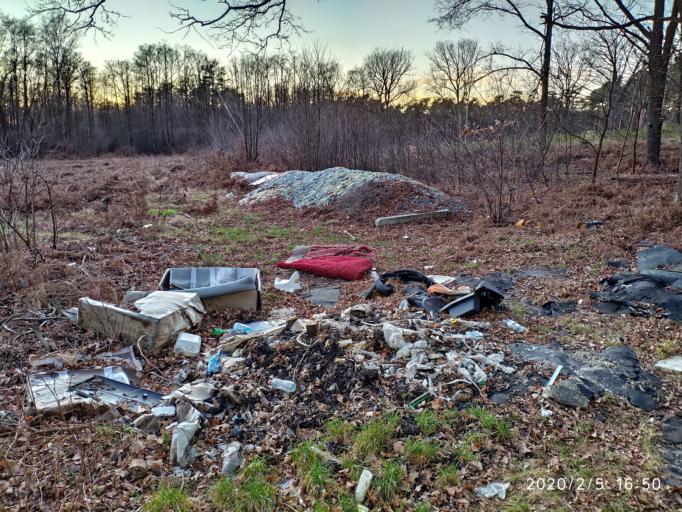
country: PL
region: Lubusz
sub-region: Zielona Gora
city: Zielona Gora
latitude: 51.9260
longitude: 15.5726
